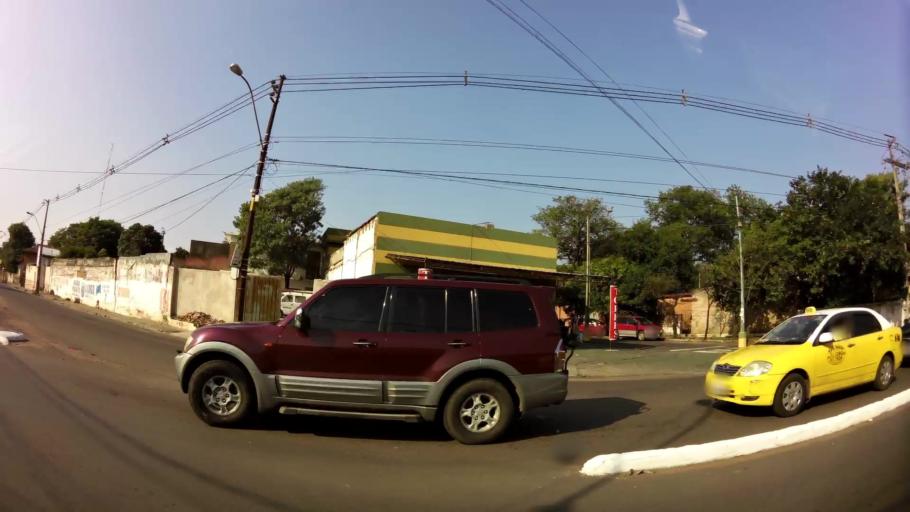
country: PY
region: Asuncion
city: Asuncion
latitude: -25.3069
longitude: -57.6187
